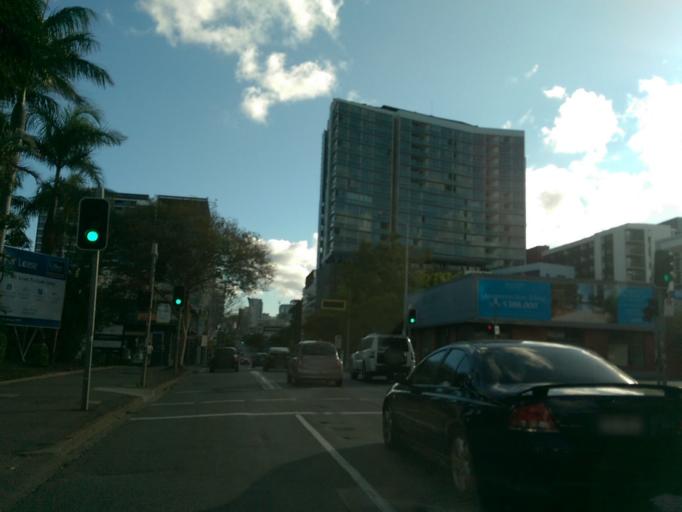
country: AU
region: Queensland
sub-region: Brisbane
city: Fortitude Valley
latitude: -27.4541
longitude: 153.0392
